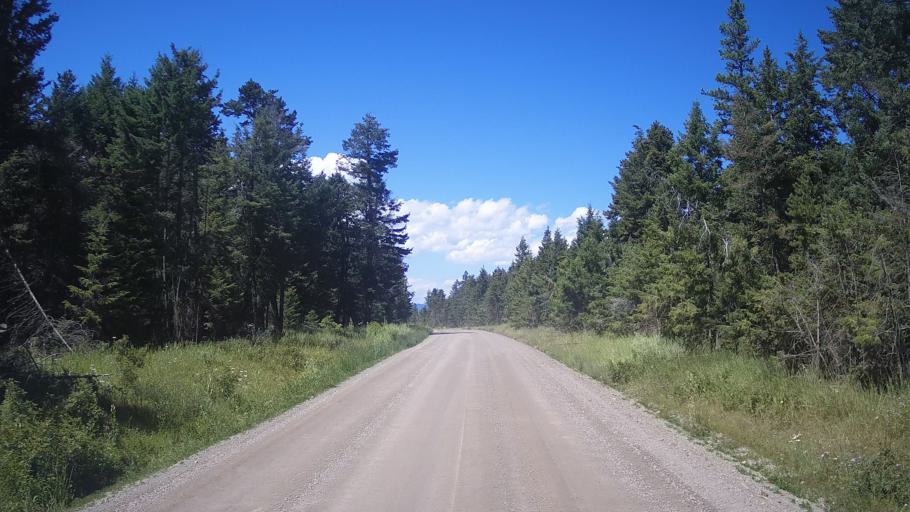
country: CA
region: British Columbia
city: Cache Creek
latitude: 51.1514
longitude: -121.5347
